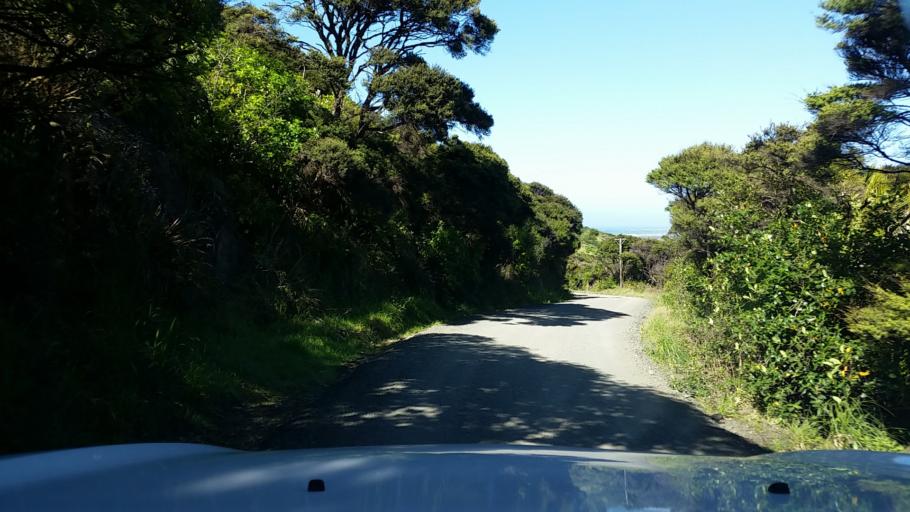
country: NZ
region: Auckland
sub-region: Auckland
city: Titirangi
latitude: -37.0348
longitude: 174.5155
